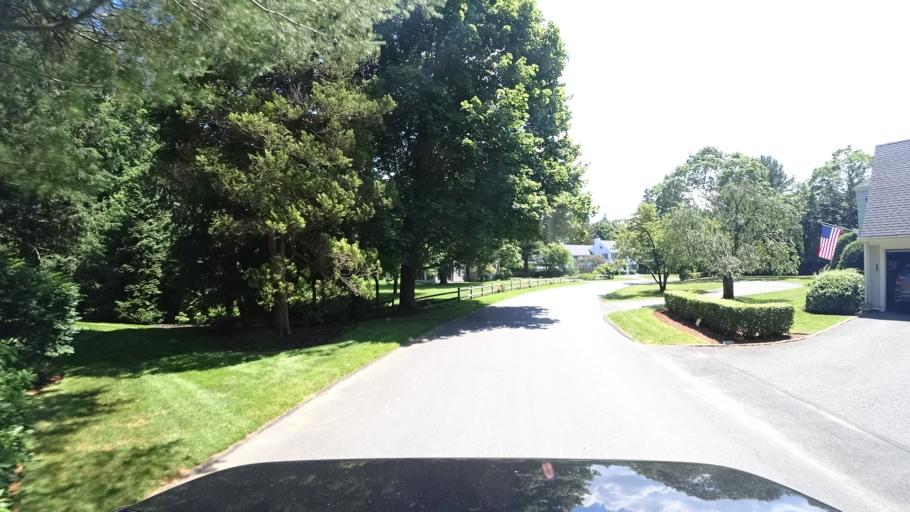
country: US
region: Massachusetts
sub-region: Norfolk County
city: Dedham
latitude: 42.2481
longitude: -71.1857
